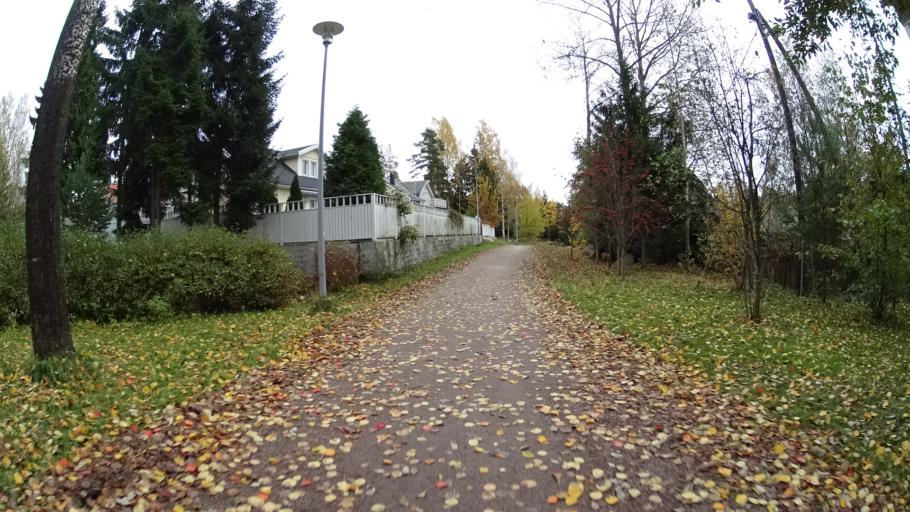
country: FI
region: Uusimaa
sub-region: Helsinki
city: Kauniainen
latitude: 60.2035
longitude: 24.7148
